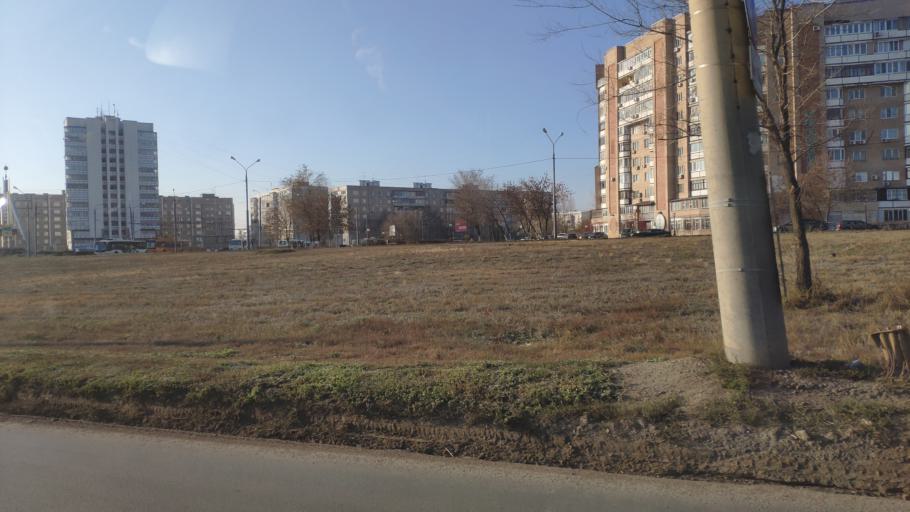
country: RU
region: Orenburg
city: Prigorodnyy
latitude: 51.7753
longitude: 55.1932
